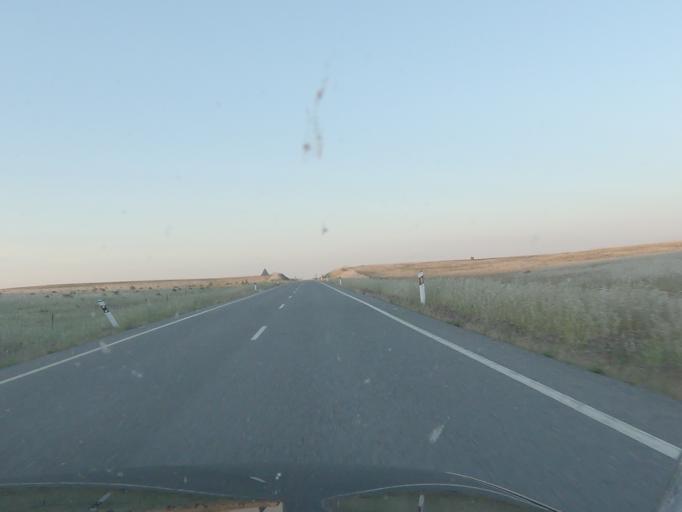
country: ES
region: Extremadura
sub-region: Provincia de Caceres
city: Alcantara
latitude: 39.6178
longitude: -6.9414
